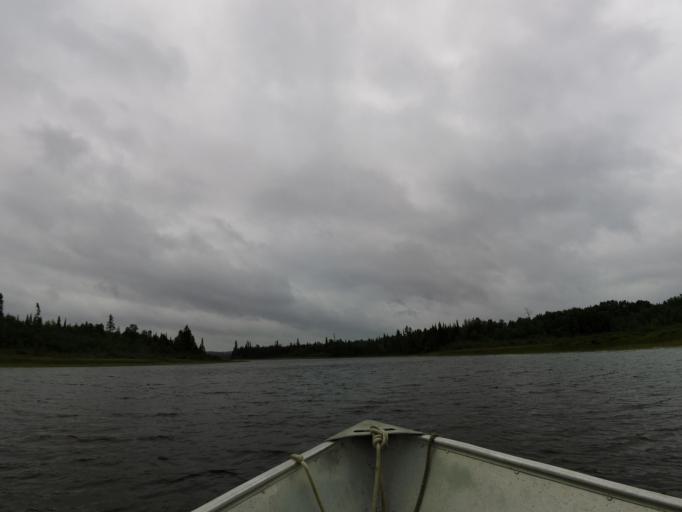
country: CA
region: Ontario
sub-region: Rainy River District
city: Atikokan
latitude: 49.5970
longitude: -91.3408
